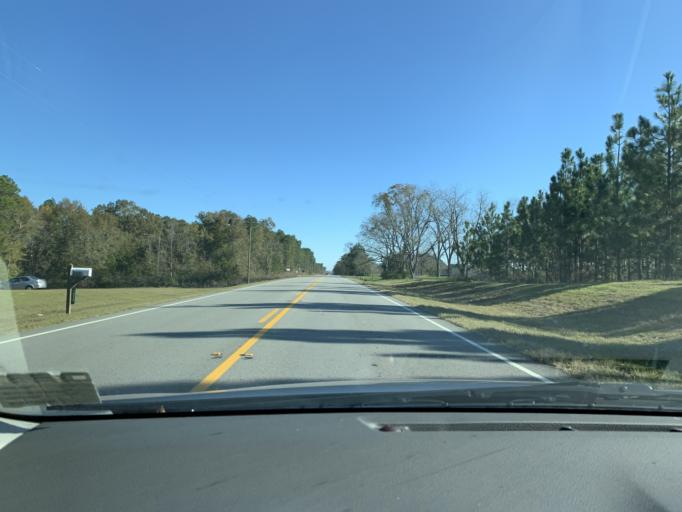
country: US
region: Georgia
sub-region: Ben Hill County
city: Fitzgerald
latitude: 31.7348
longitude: -83.1661
